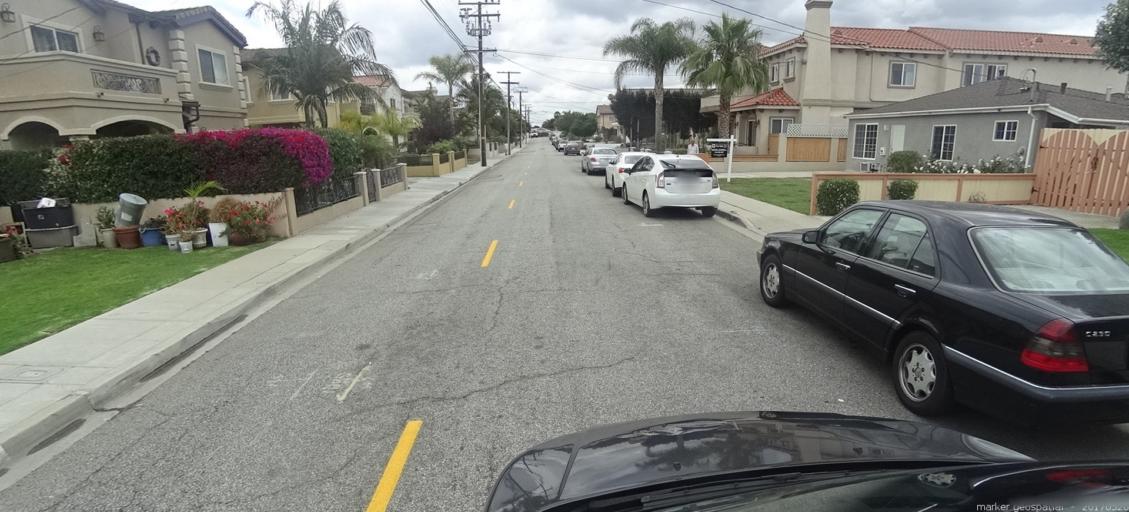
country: US
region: California
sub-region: Los Angeles County
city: Lawndale
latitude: 33.8865
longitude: -118.3724
